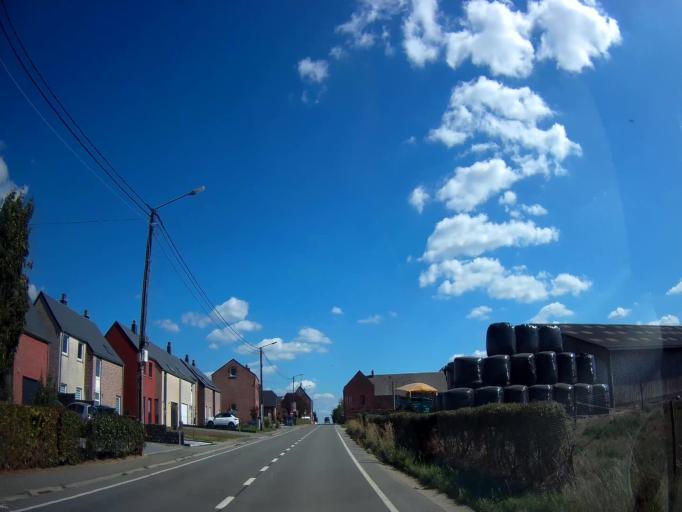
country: FR
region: Champagne-Ardenne
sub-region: Departement des Ardennes
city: Fromelennes
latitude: 50.1659
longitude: 4.8881
